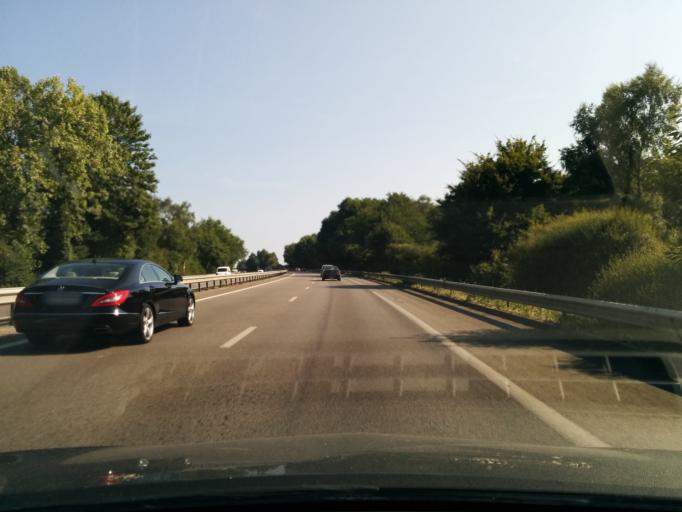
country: FR
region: Limousin
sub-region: Departement de la Haute-Vienne
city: Condat-sur-Vienne
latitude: 45.7866
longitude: 1.3029
